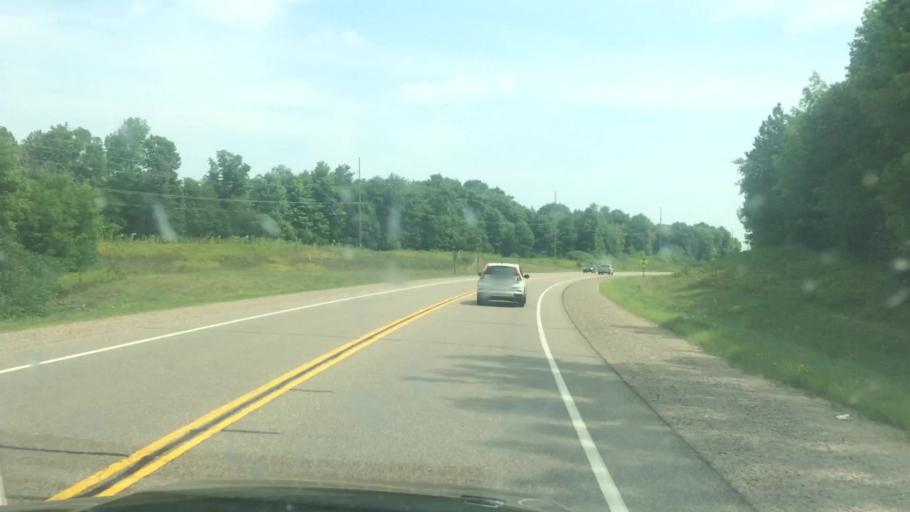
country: US
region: Wisconsin
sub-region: Langlade County
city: Antigo
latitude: 45.1677
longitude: -89.0093
